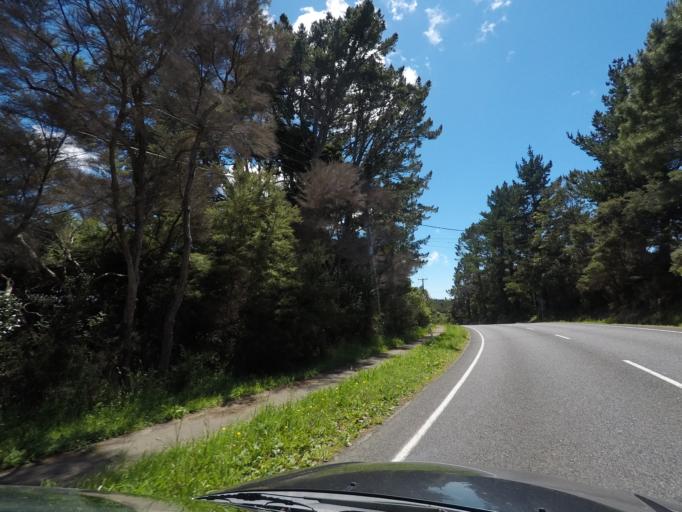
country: NZ
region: Auckland
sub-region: Auckland
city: Rothesay Bay
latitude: -36.7514
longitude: 174.6687
